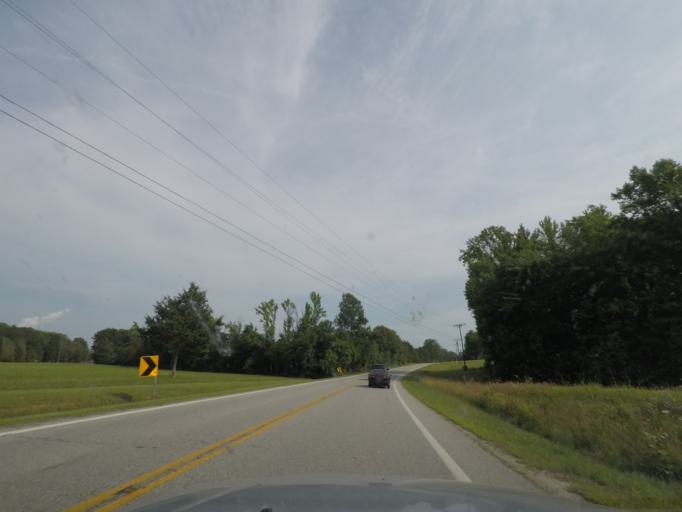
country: US
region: Virginia
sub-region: Prince Edward County
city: Hampden Sydney
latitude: 37.1972
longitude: -78.4302
